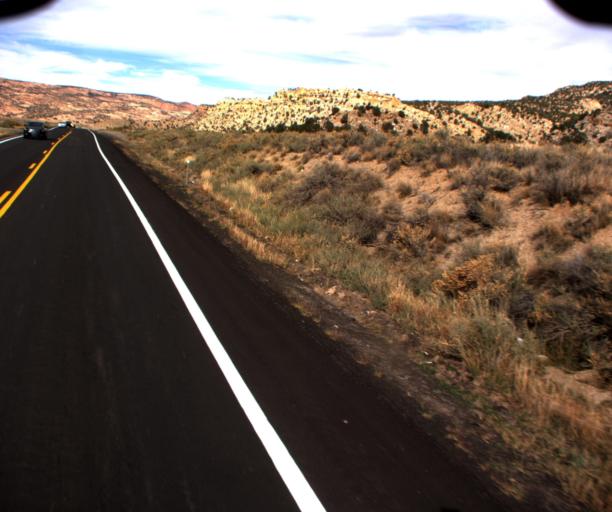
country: US
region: Arizona
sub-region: Navajo County
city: Kayenta
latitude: 36.5928
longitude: -110.4722
